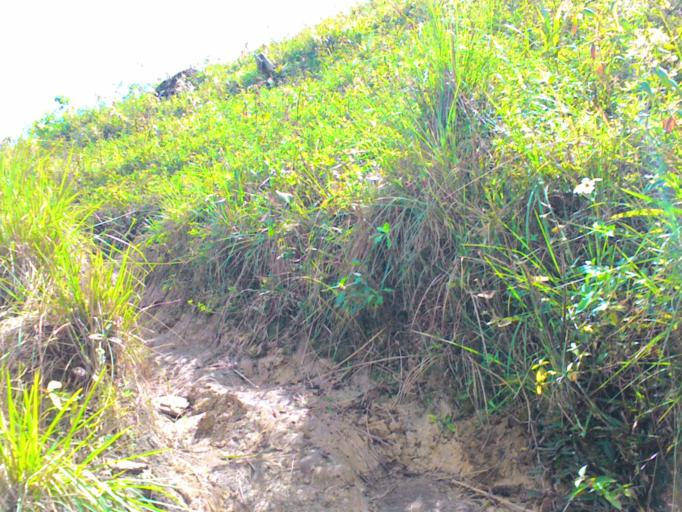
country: HT
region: Sud
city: Les Anglais
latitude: 18.4499
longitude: -74.1050
